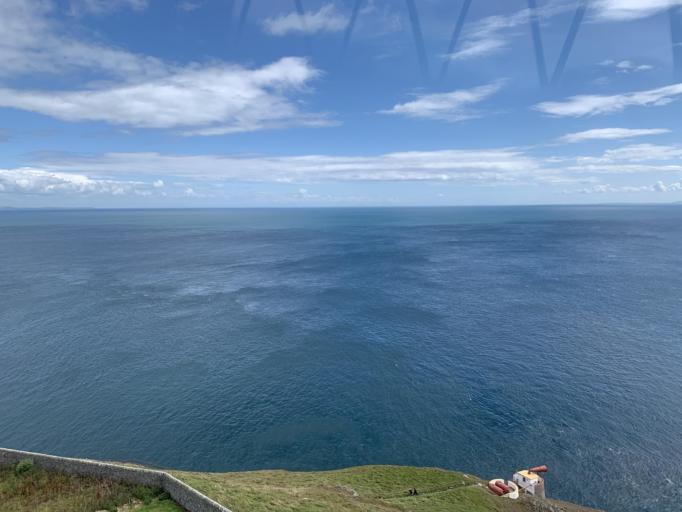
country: GB
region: Scotland
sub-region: Dumfries and Galloway
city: Stranraer
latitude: 54.6350
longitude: -4.8571
